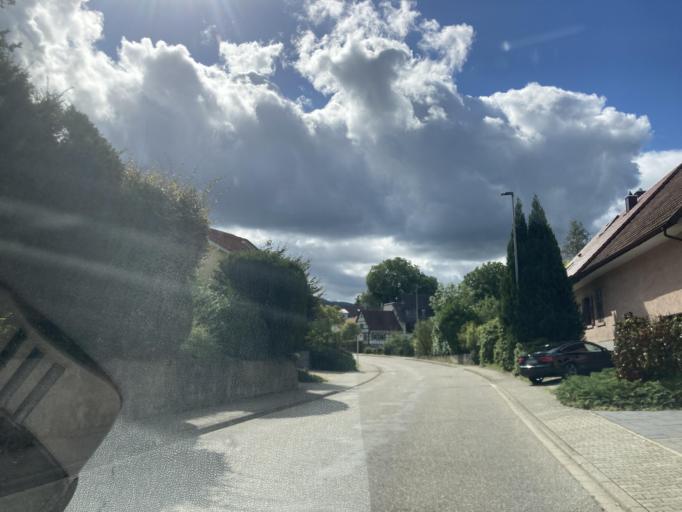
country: DE
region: Baden-Wuerttemberg
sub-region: Karlsruhe Region
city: Buhl
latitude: 48.6867
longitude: 8.1472
